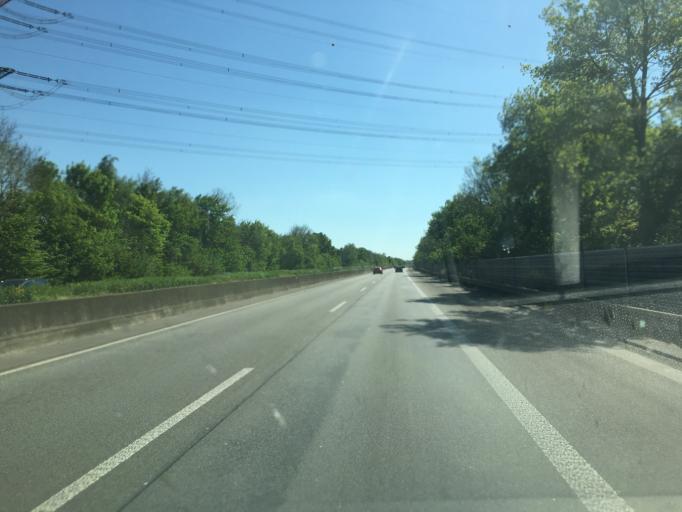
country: DE
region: North Rhine-Westphalia
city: Castrop-Rauxel
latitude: 51.5751
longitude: 7.3641
